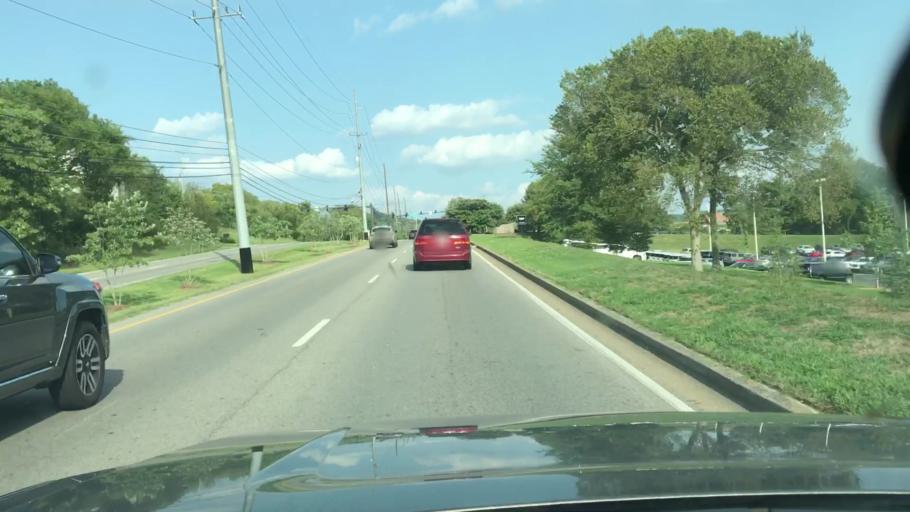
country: US
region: Tennessee
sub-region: Williamson County
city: Brentwood
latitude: 36.0378
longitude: -86.7967
